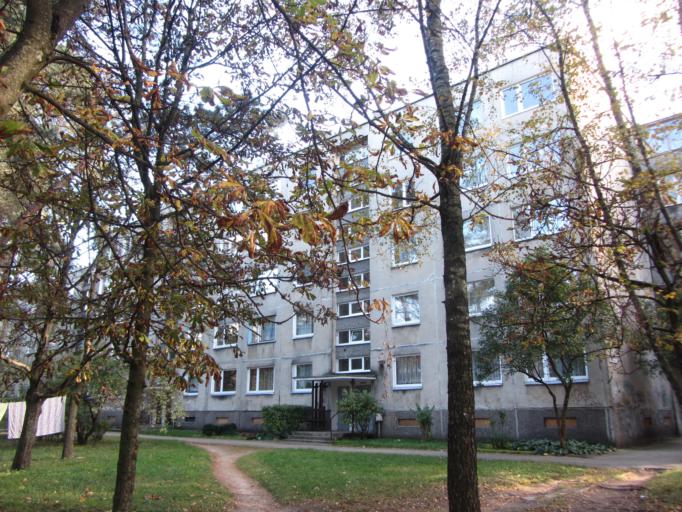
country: LT
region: Vilnius County
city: Lazdynai
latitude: 54.6774
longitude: 25.2170
